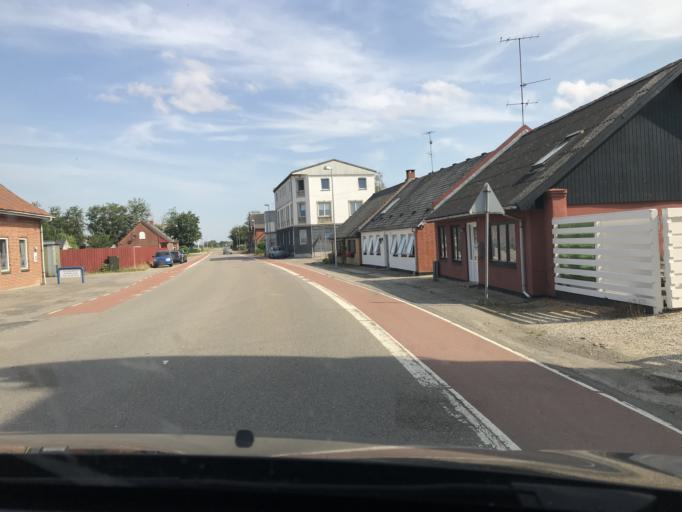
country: DK
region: Central Jutland
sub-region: Norddjurs Kommune
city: Allingabro
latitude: 56.4645
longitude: 10.3190
